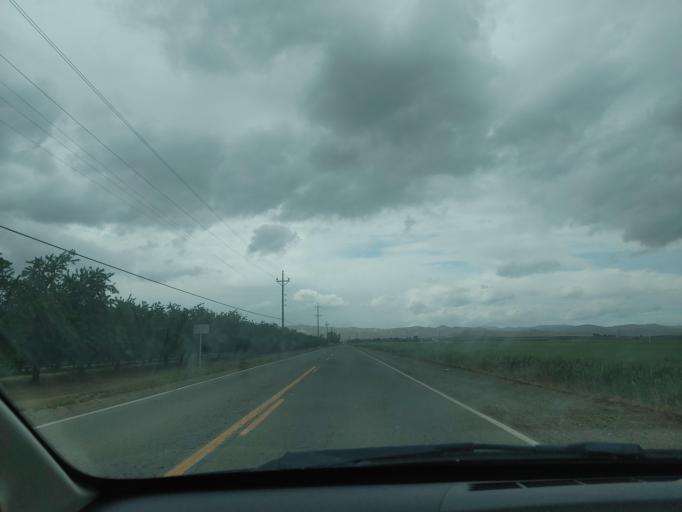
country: US
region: California
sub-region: Stanislaus County
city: Newman
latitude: 37.3334
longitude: -121.0691
